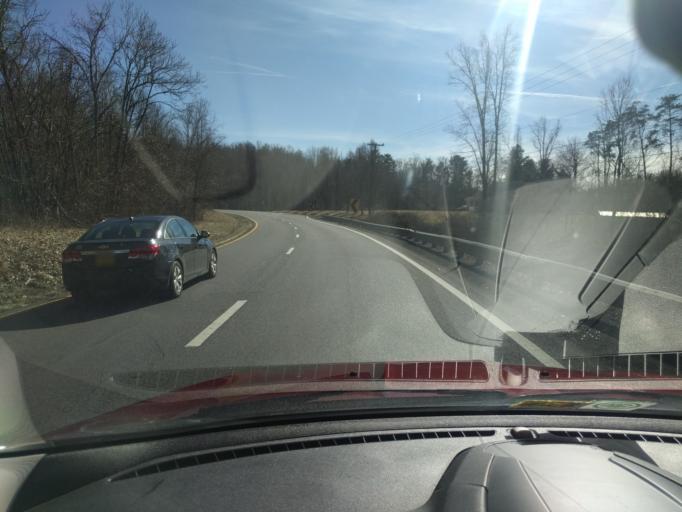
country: US
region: Virginia
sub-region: Botetourt County
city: Blue Ridge
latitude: 37.3663
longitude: -79.6940
